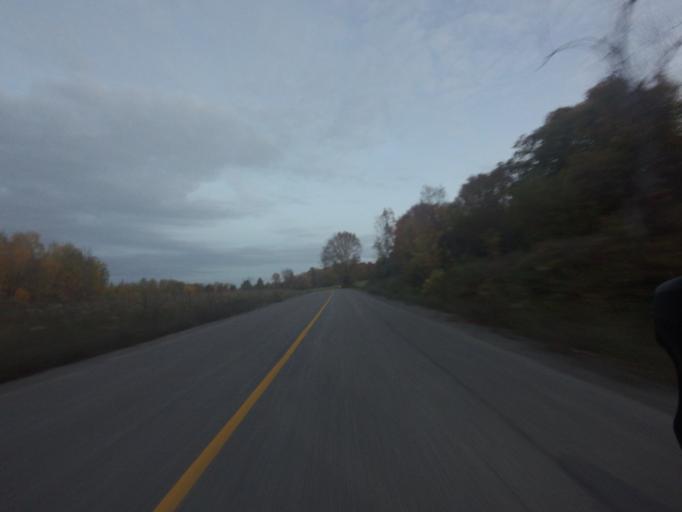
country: CA
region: Ontario
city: Renfrew
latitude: 45.3417
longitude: -76.9203
